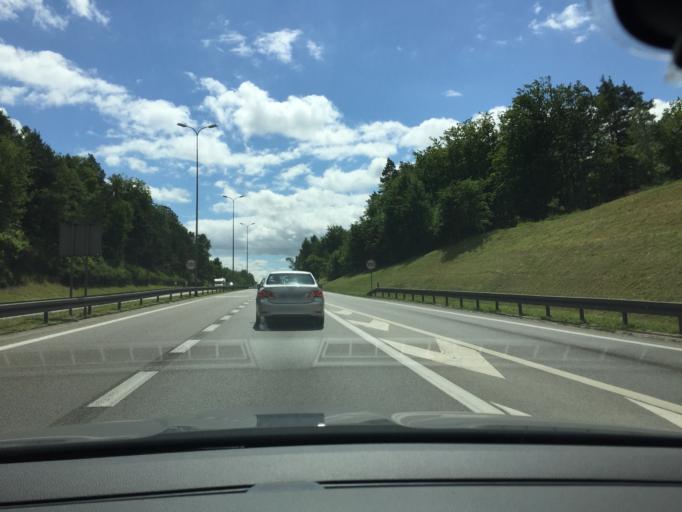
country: PL
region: Pomeranian Voivodeship
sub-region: Gdynia
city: Wielki Kack
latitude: 54.5103
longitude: 18.4578
